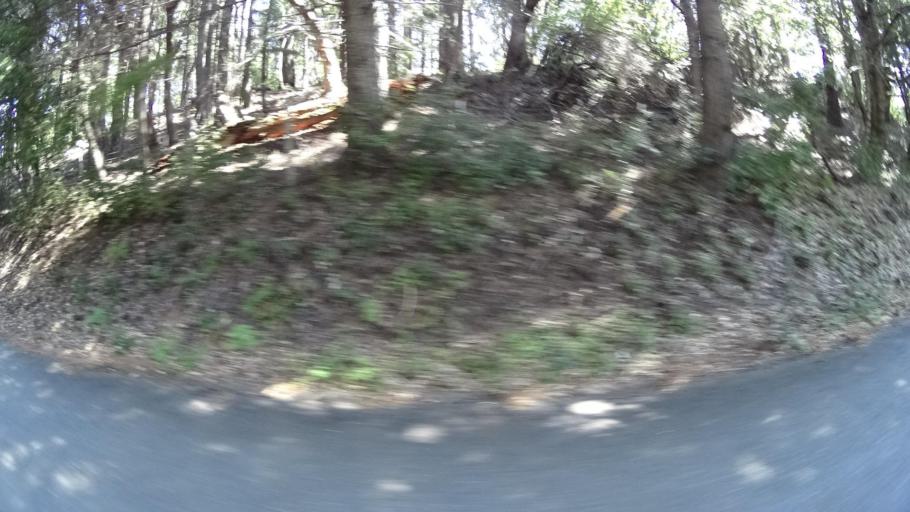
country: US
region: California
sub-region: Humboldt County
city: Redway
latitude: 40.1677
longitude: -124.0846
